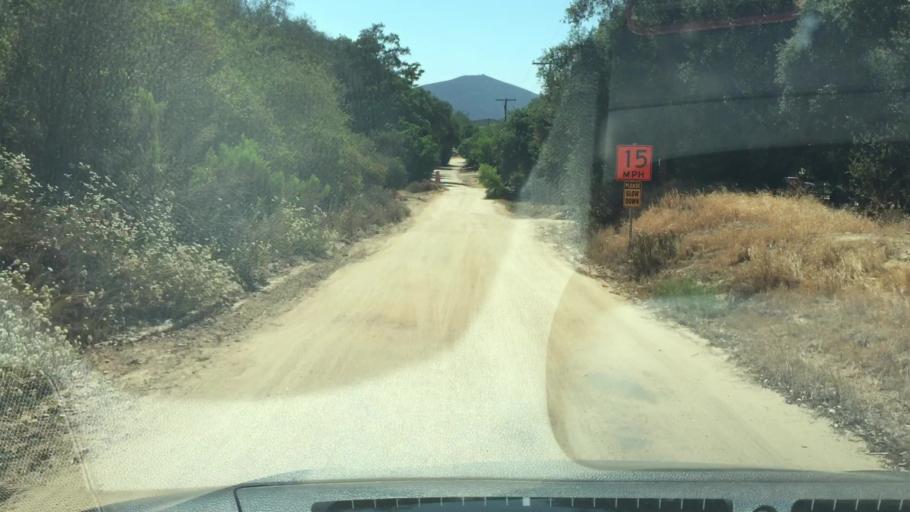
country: US
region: California
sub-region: San Diego County
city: Alpine
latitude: 32.7538
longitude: -116.7517
